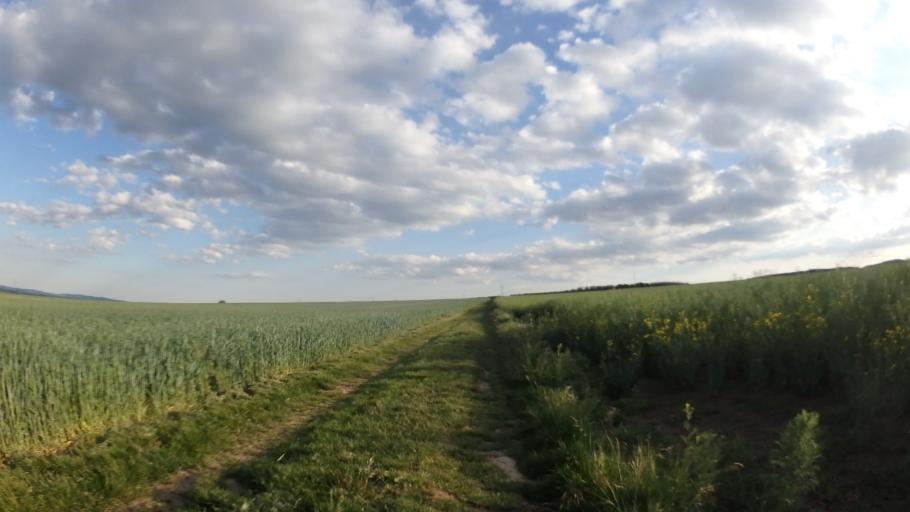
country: CZ
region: South Moravian
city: Moravany
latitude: 49.1390
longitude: 16.5915
